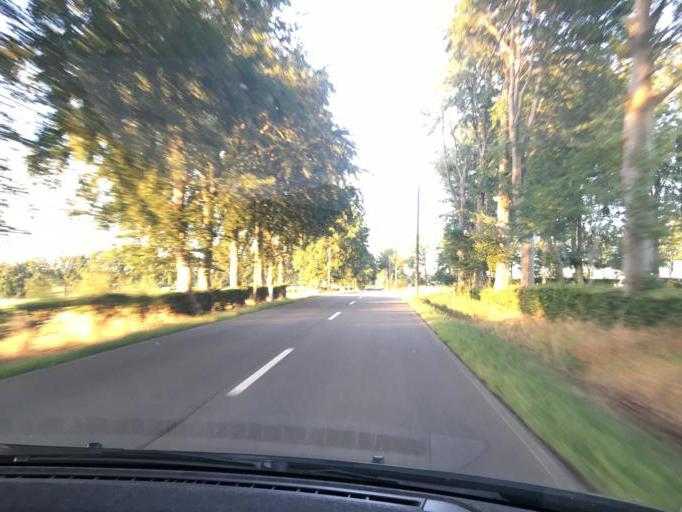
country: DE
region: North Rhine-Westphalia
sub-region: Regierungsbezirk Koln
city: Simmerath
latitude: 50.6434
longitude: 6.3230
